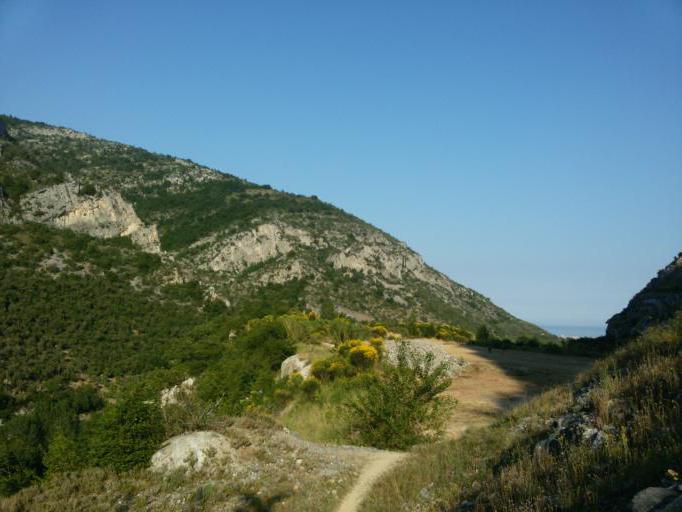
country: IT
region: Liguria
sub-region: Provincia di Savona
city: Toirano
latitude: 44.1369
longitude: 8.1934
